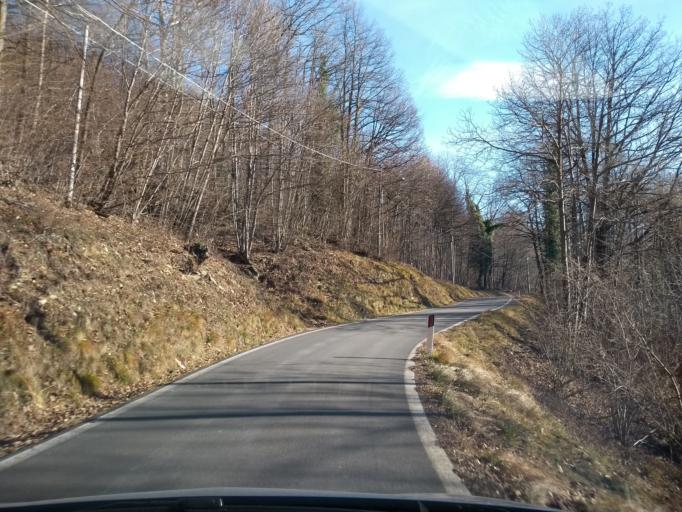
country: IT
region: Piedmont
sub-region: Provincia di Torino
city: Traves
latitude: 45.2834
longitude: 7.4359
